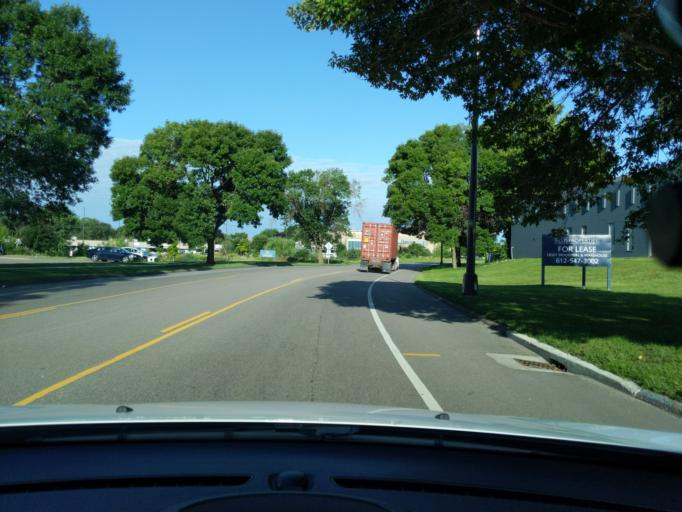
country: US
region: Minnesota
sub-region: Ramsey County
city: Falcon Heights
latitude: 44.9648
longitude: -93.1378
